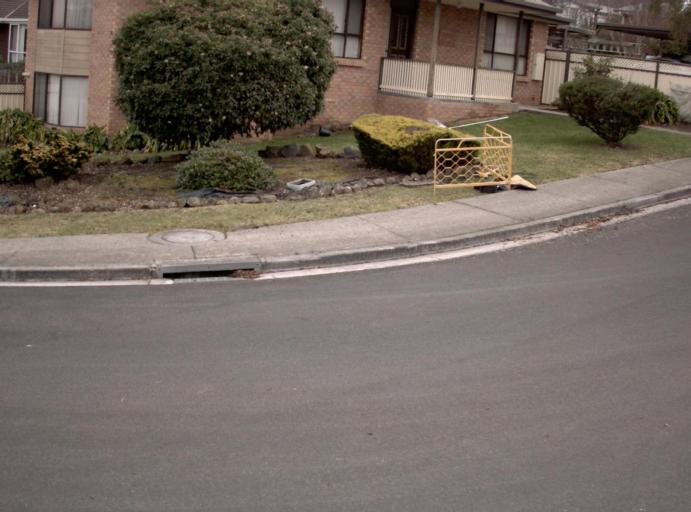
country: AU
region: Tasmania
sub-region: Launceston
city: Newstead
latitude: -41.4640
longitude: 147.1802
